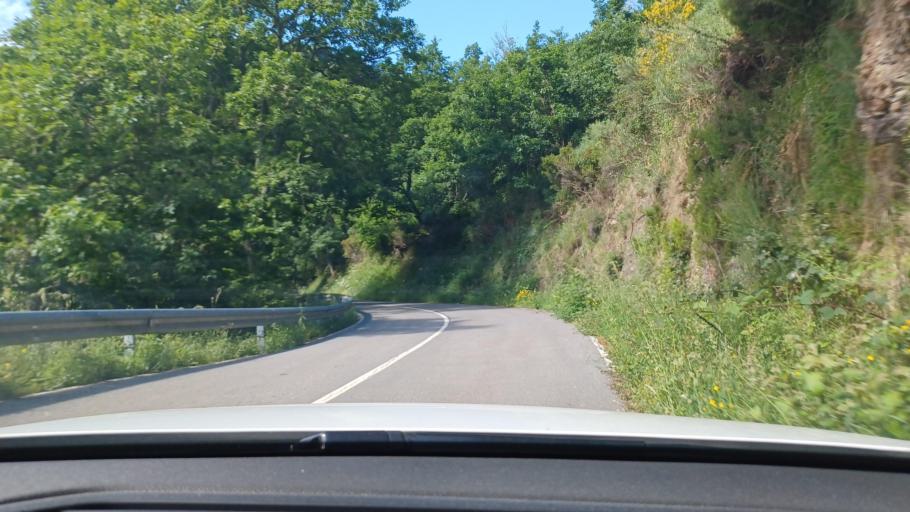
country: ES
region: Asturias
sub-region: Province of Asturias
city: La Plaza
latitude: 43.0983
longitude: -6.0430
